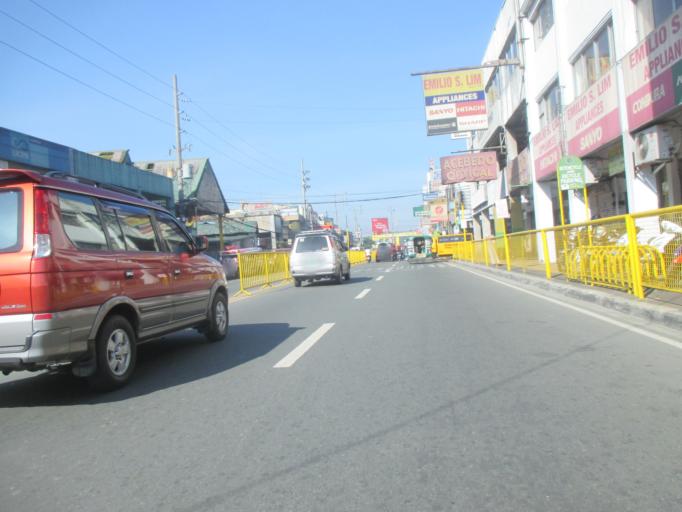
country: PH
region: Metro Manila
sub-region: Marikina
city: Calumpang
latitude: 14.6358
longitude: 121.0961
